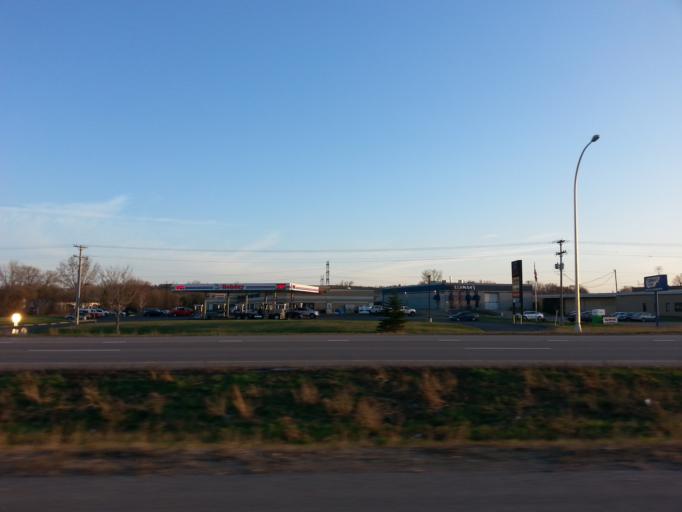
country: US
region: Minnesota
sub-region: Scott County
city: Savage
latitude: 44.7807
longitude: -93.3864
